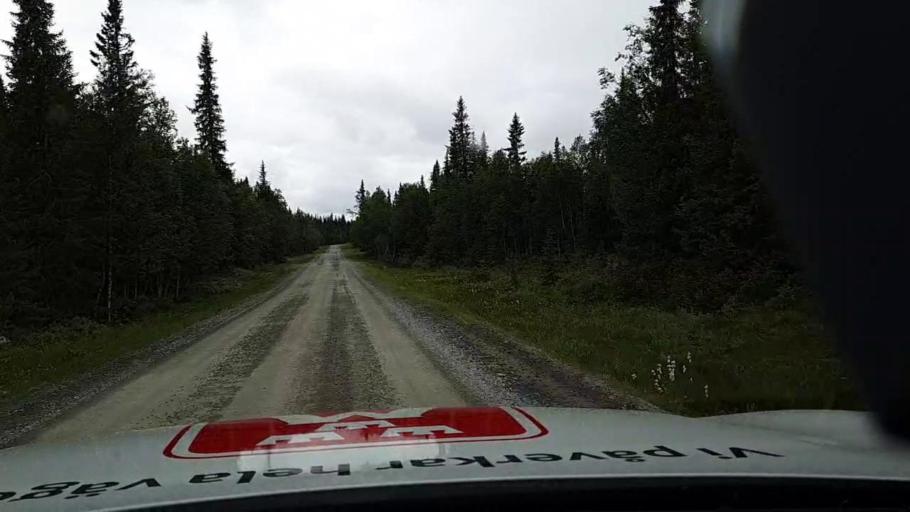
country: SE
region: Jaemtland
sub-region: Bergs Kommun
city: Hoverberg
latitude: 62.8515
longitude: 13.8722
